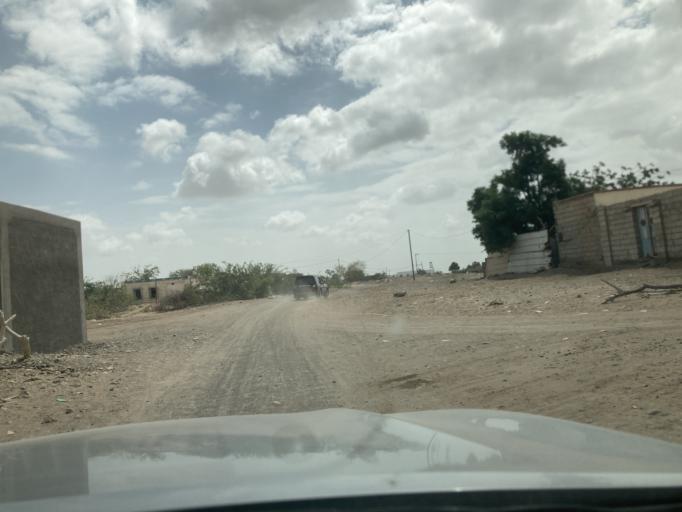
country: YE
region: Lahij
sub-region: Al  Hawtah
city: Lahij
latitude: 13.0191
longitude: 45.0028
